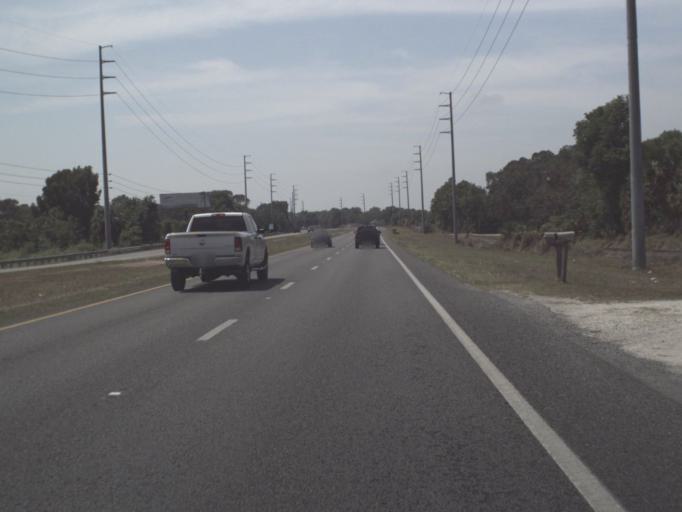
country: US
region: Florida
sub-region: Lake County
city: Umatilla
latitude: 28.9054
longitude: -81.6817
